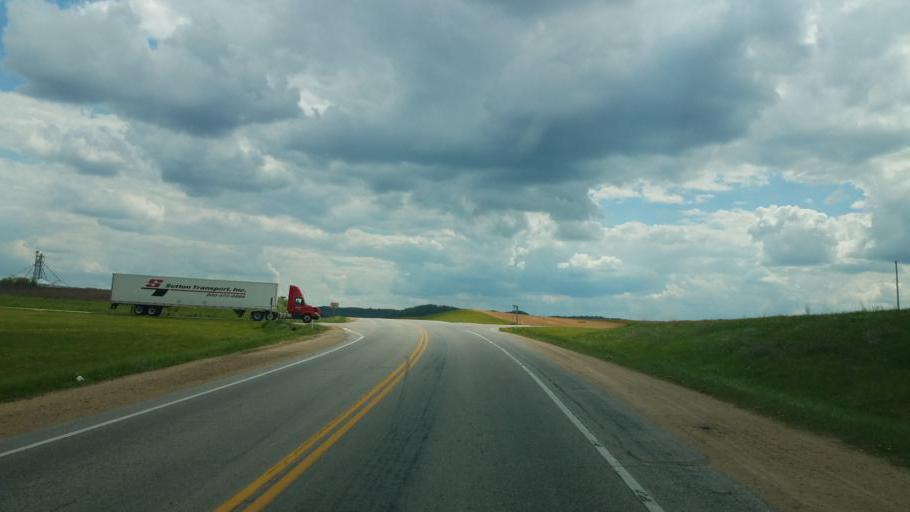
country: US
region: Wisconsin
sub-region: Vernon County
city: Hillsboro
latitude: 43.6446
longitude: -90.3571
